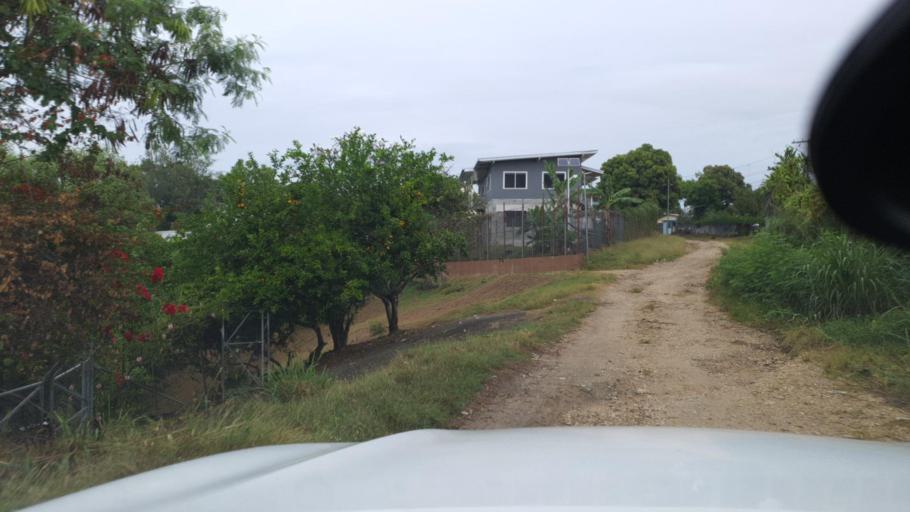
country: SB
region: Guadalcanal
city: Honiara
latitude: -9.4407
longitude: 159.9672
